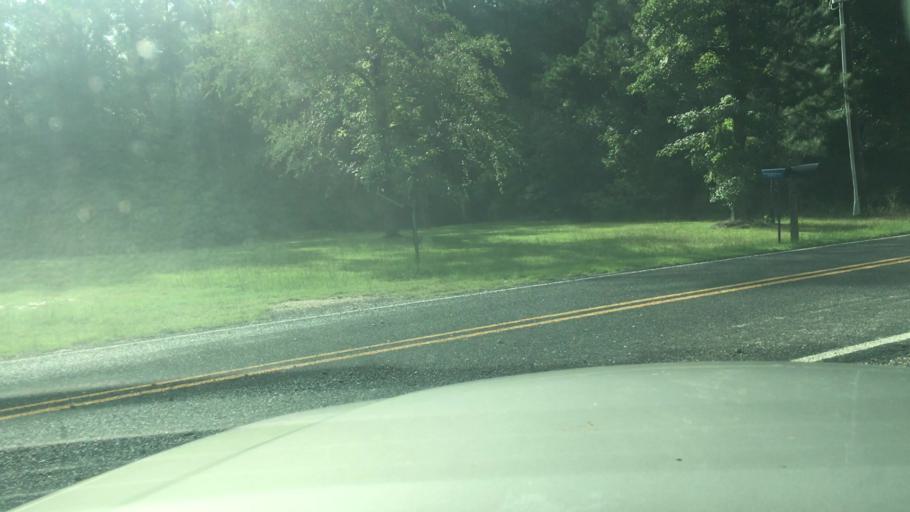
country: US
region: North Carolina
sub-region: Cumberland County
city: Eastover
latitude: 35.1568
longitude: -78.8531
